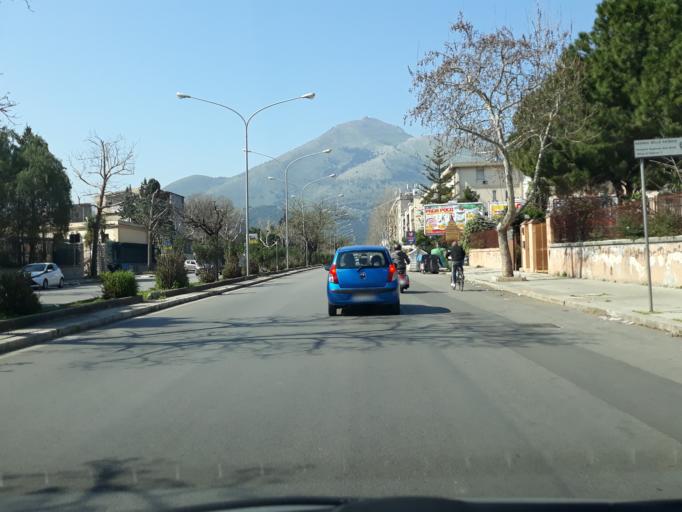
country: IT
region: Sicily
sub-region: Palermo
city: Palermo
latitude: 38.1355
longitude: 13.3147
